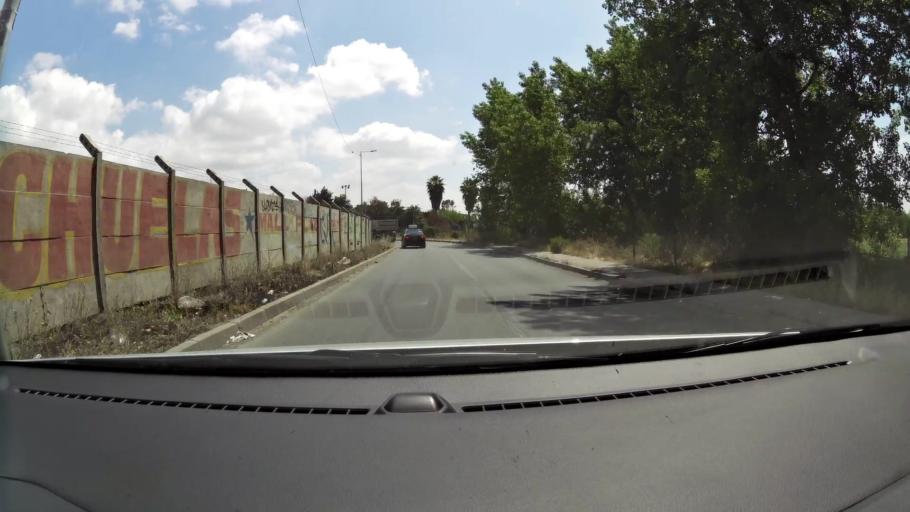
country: CL
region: Santiago Metropolitan
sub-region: Provincia de Santiago
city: Lo Prado
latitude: -33.5126
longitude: -70.7153
